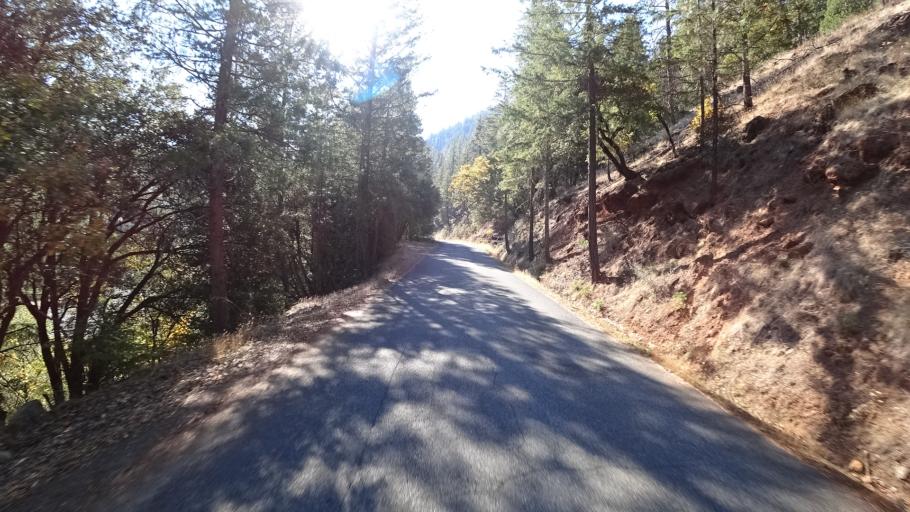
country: US
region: California
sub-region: Siskiyou County
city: Happy Camp
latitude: 41.7577
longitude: -123.0144
